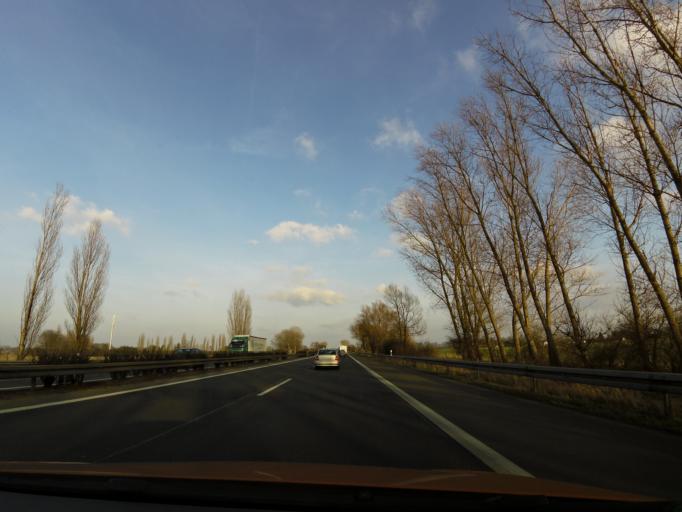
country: DE
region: Brandenburg
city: Velten
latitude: 52.7067
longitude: 13.1267
